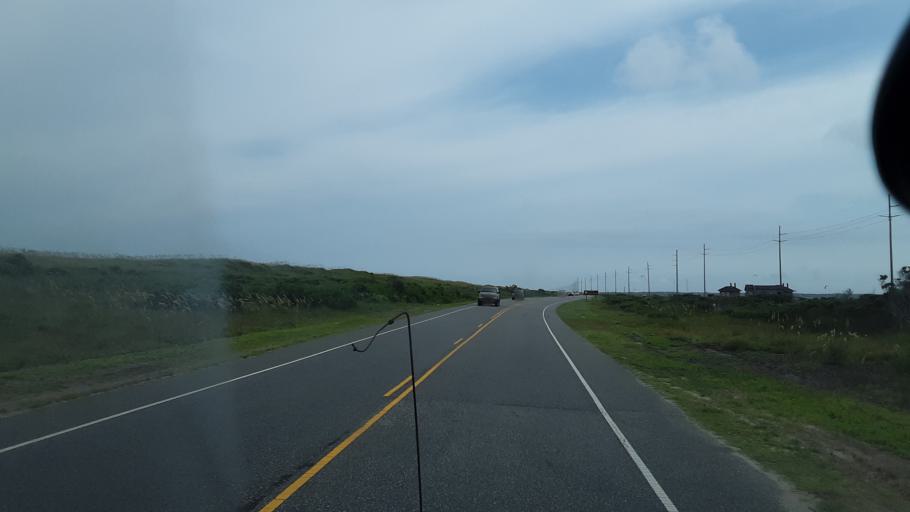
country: US
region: North Carolina
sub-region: Dare County
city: Buxton
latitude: 35.3012
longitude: -75.5136
